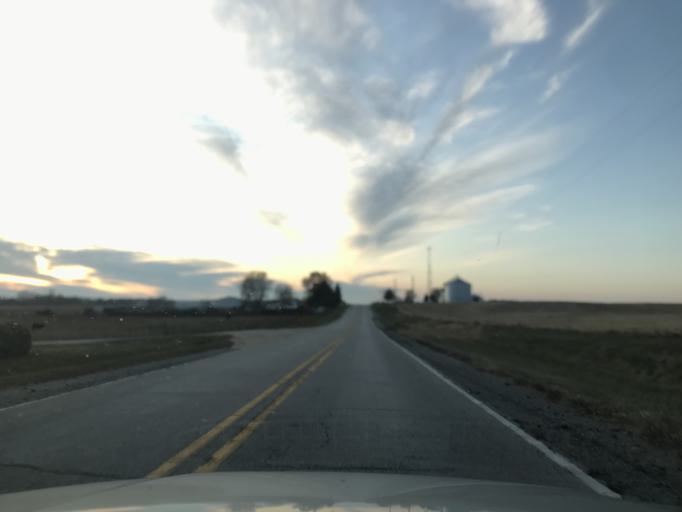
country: US
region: Illinois
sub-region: Henderson County
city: Oquawka
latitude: 41.0188
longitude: -90.8400
